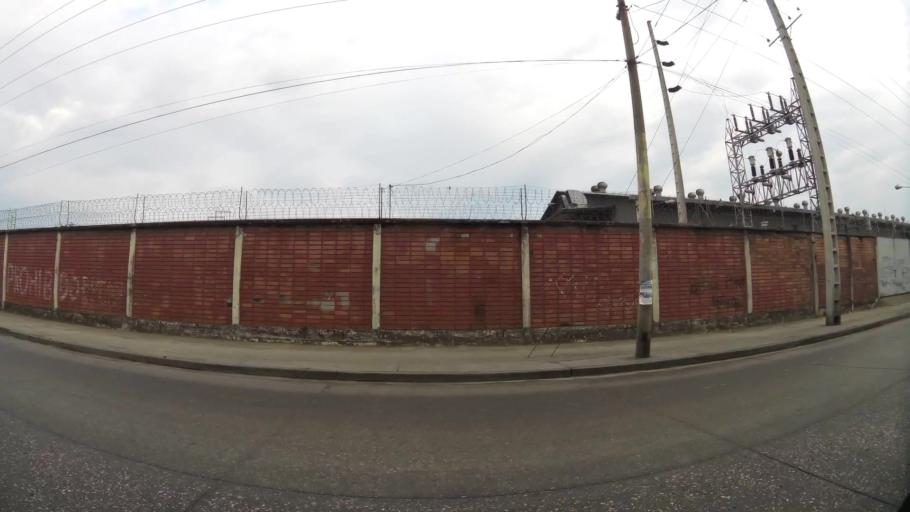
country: EC
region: Guayas
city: Guayaquil
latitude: -2.2419
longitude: -79.8860
